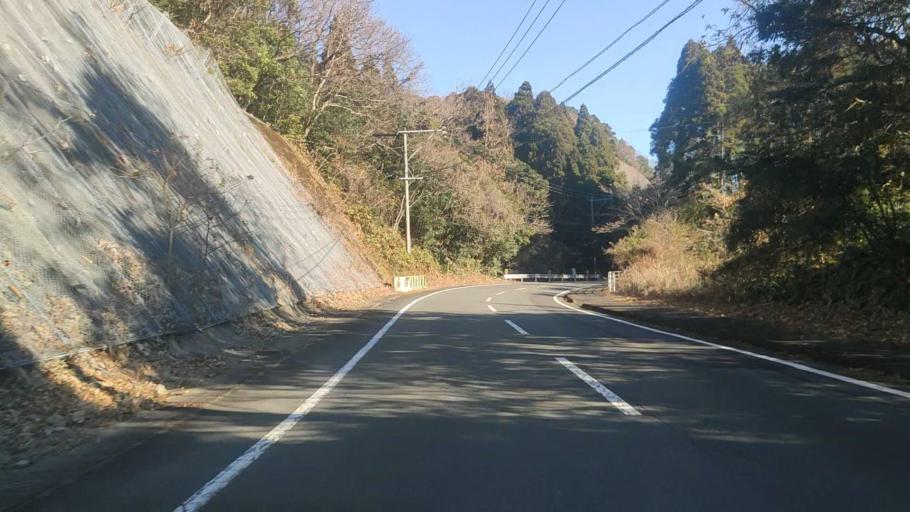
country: JP
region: Miyazaki
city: Nobeoka
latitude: 32.6863
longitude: 131.8039
